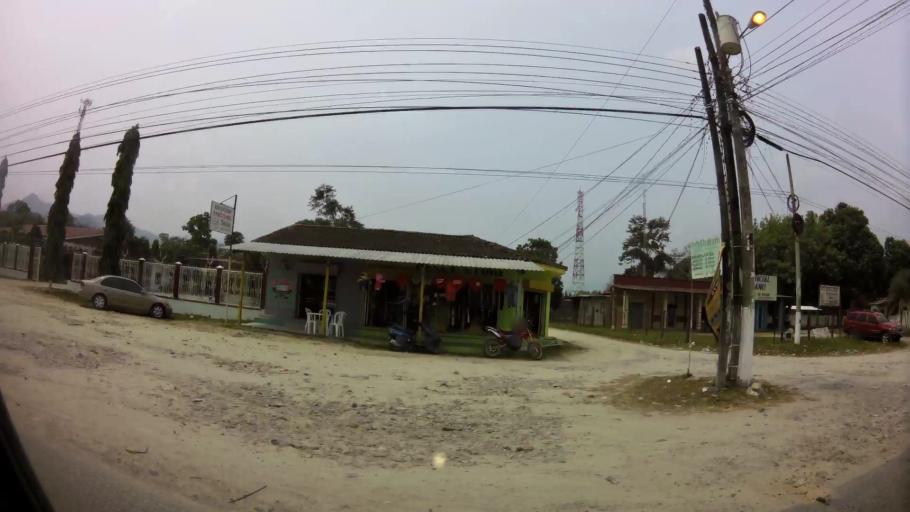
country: HN
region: Atlantida
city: San Juan Pueblo
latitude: 15.5992
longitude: -87.2071
